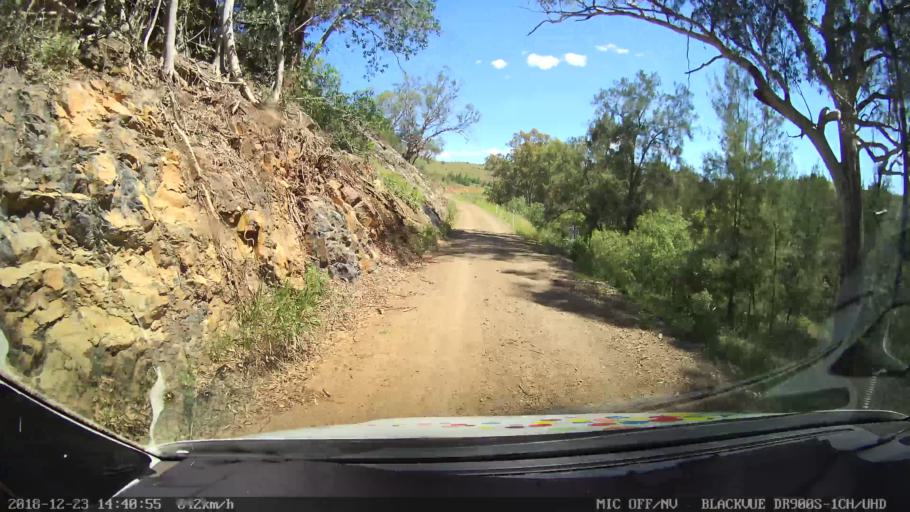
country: AU
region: New South Wales
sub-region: Tamworth Municipality
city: Manilla
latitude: -30.6286
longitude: 150.9029
